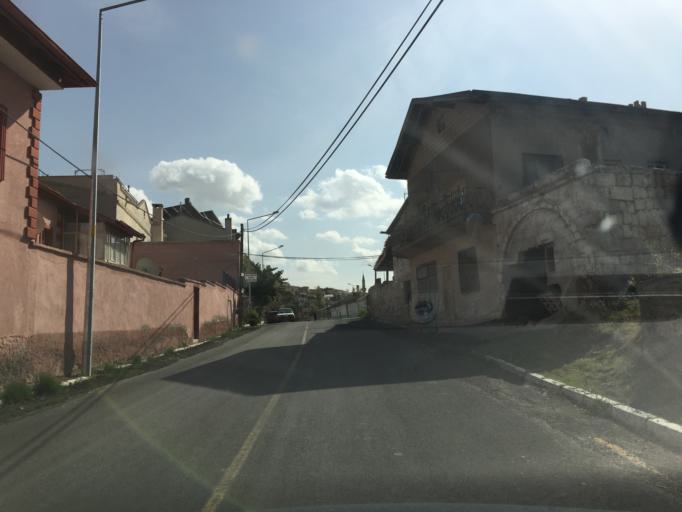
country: TR
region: Nevsehir
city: Goereme
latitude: 38.6700
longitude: 34.8407
